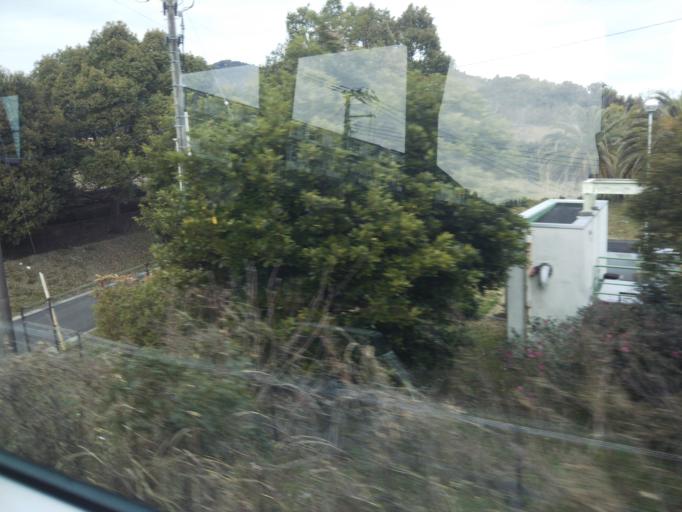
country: JP
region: Kochi
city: Nakamura
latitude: 32.9809
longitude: 132.9470
